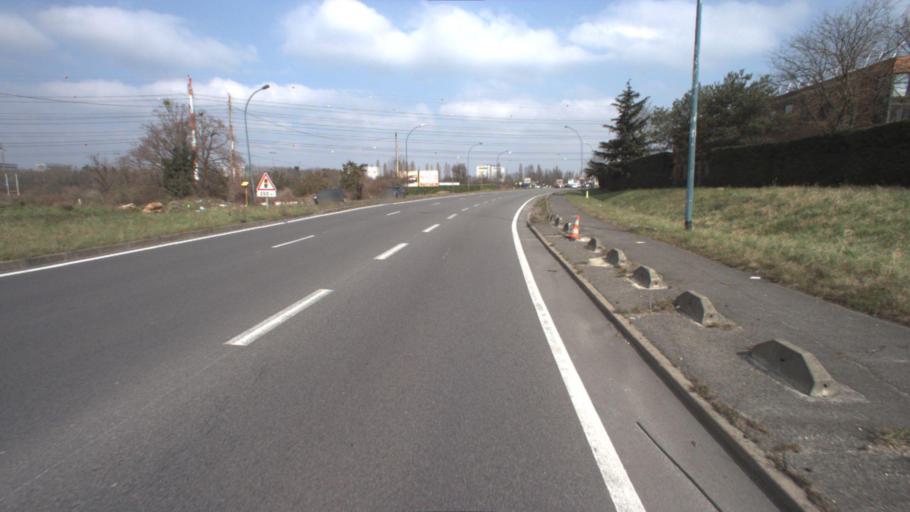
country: FR
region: Ile-de-France
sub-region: Departement de l'Essonne
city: Massy
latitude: 48.7275
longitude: 2.3004
